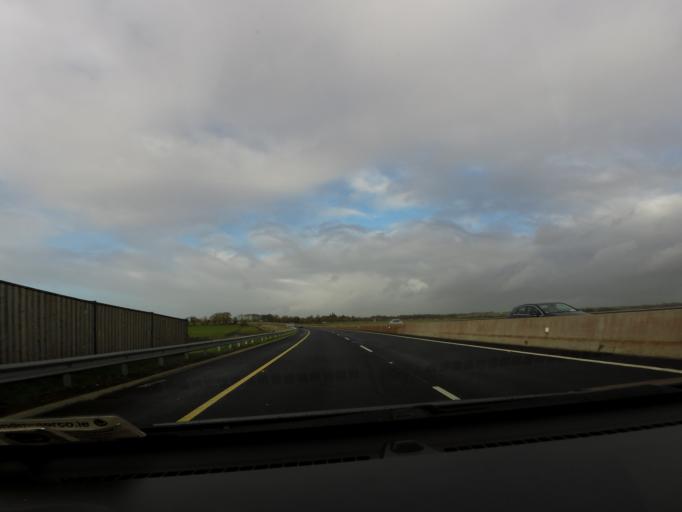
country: IE
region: Connaught
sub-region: County Galway
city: Tuam
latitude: 53.4582
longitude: -8.8479
